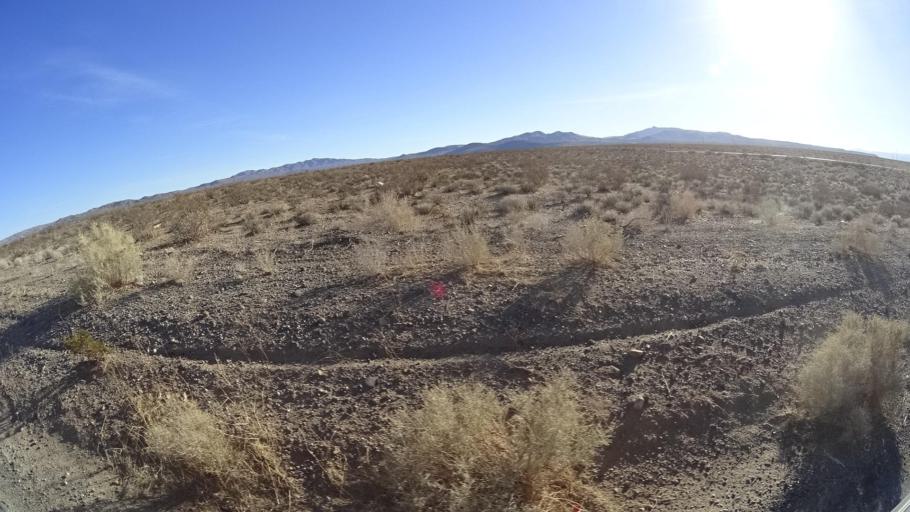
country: US
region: California
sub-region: Kern County
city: China Lake Acres
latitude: 35.6076
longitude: -117.7607
